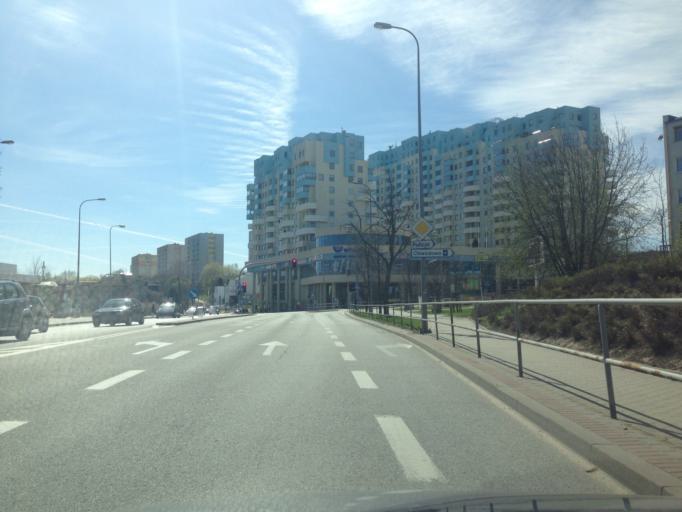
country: PL
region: Pomeranian Voivodeship
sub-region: Gdynia
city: Gdynia
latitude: 54.4989
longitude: 18.5106
